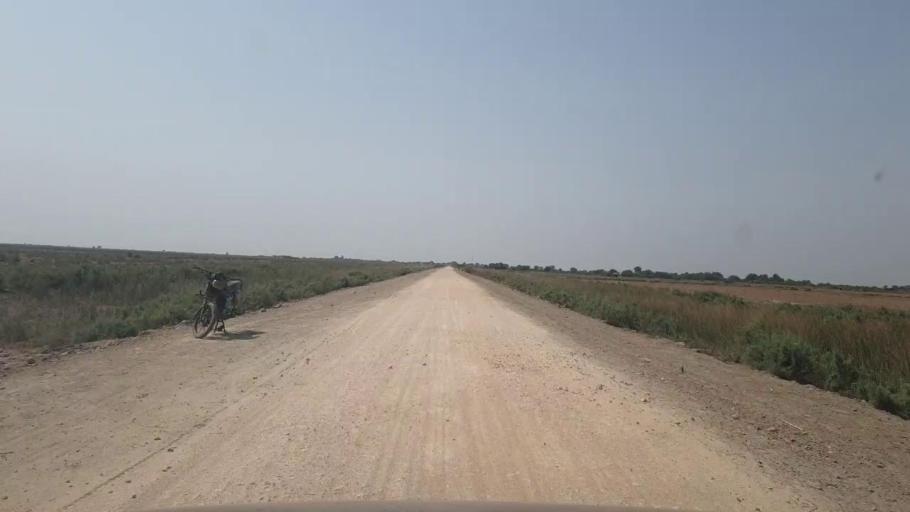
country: PK
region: Sindh
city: Jati
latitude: 24.3683
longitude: 68.5621
